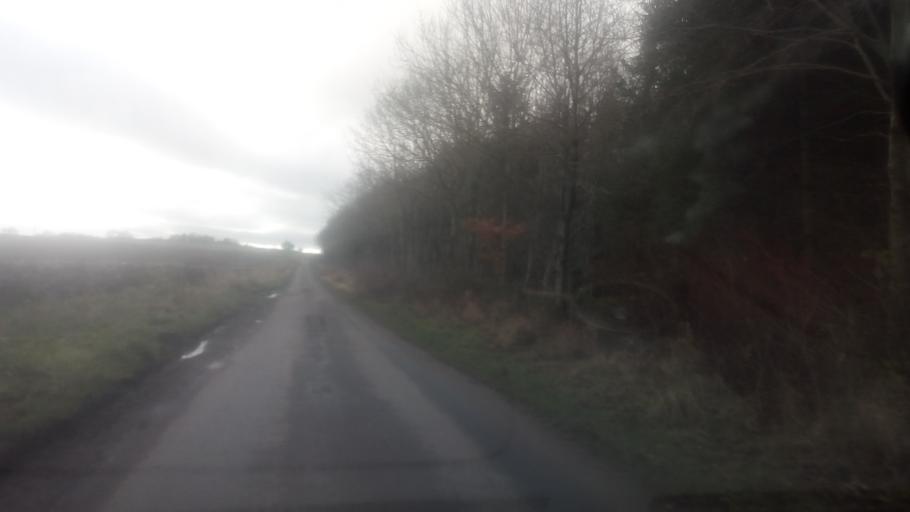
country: GB
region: Scotland
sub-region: The Scottish Borders
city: Kelso
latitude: 55.5633
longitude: -2.4817
